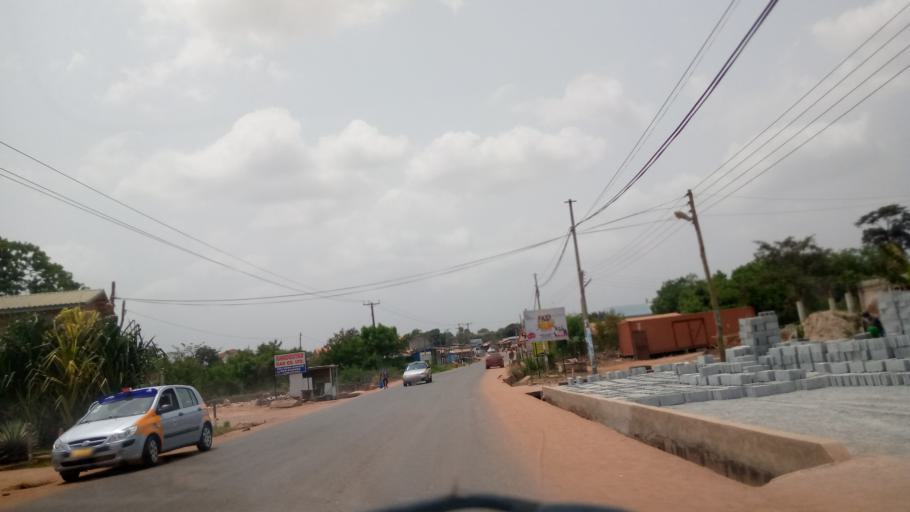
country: GH
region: Greater Accra
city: Dome
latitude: 5.6720
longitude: -0.2045
